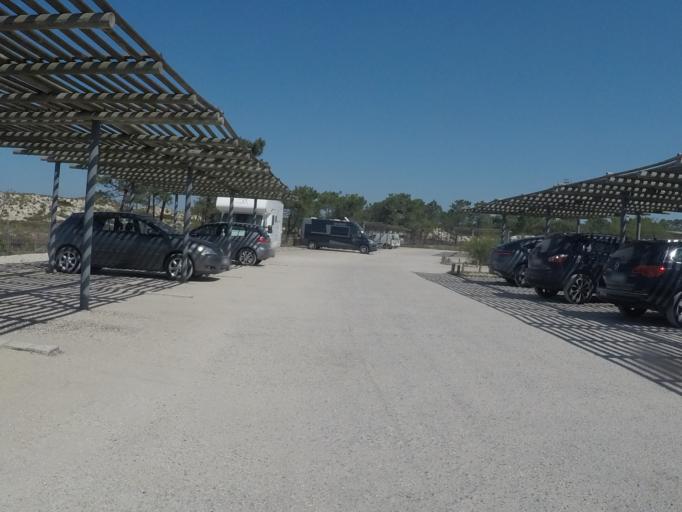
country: PT
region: Setubal
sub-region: Setubal
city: Setubal
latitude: 38.3823
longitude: -8.8018
